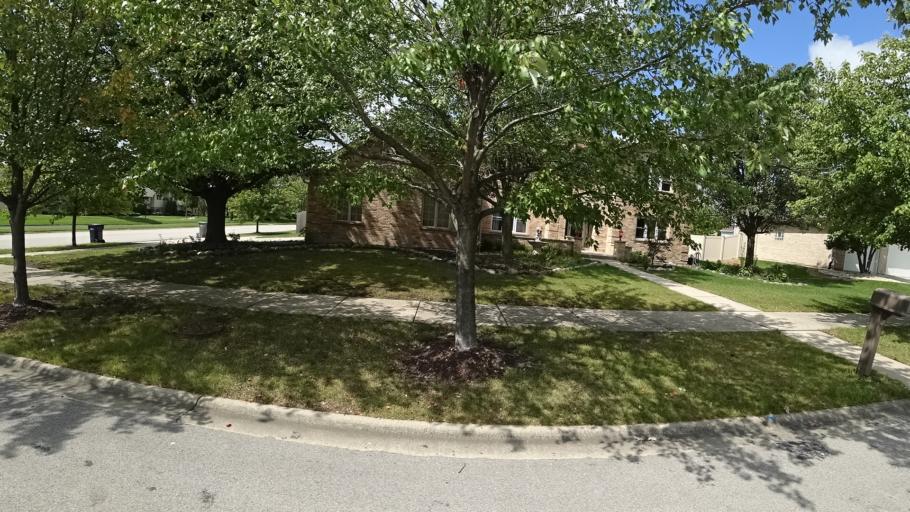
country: US
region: Illinois
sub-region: Will County
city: Mokena
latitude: 41.5607
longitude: -87.8775
